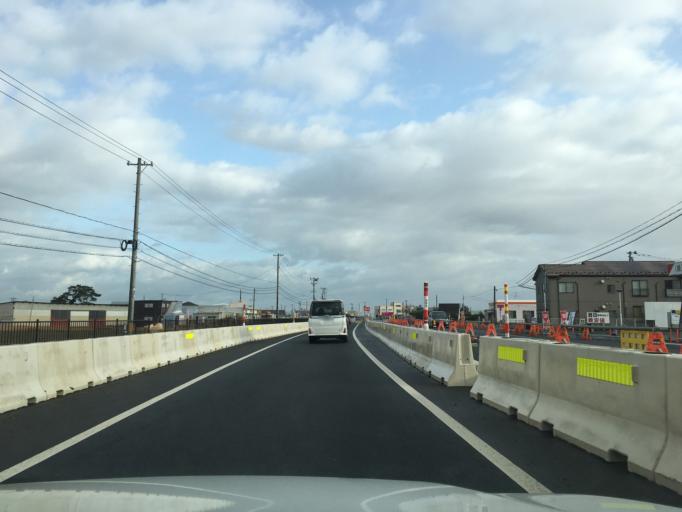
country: JP
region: Yamagata
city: Sakata
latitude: 38.8459
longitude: 139.8487
